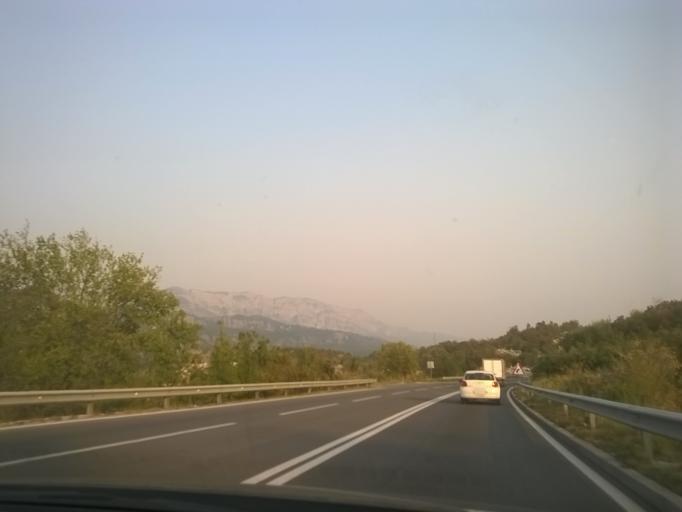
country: ME
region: Opstina Niksic
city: Niksic
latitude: 42.7070
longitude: 18.9584
